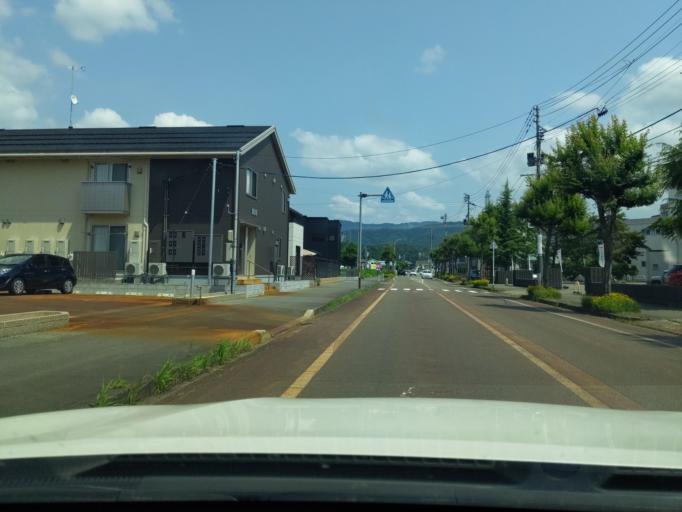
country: JP
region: Niigata
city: Nagaoka
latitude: 37.4287
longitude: 138.8572
